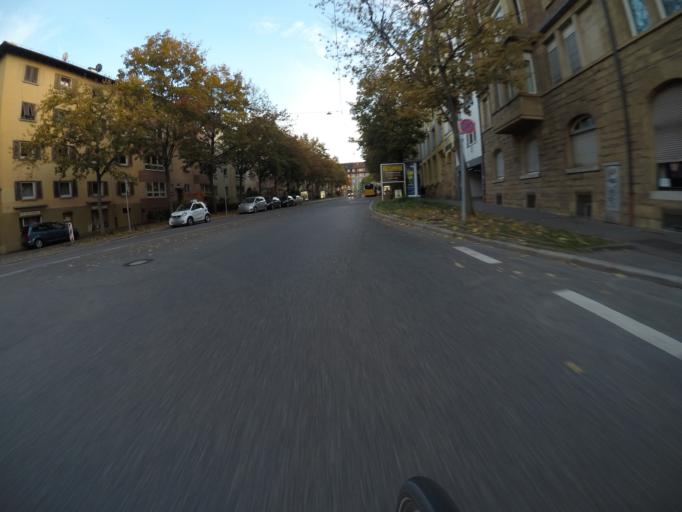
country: DE
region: Baden-Wuerttemberg
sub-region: Regierungsbezirk Stuttgart
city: Stuttgart-Ost
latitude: 48.7827
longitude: 9.2079
